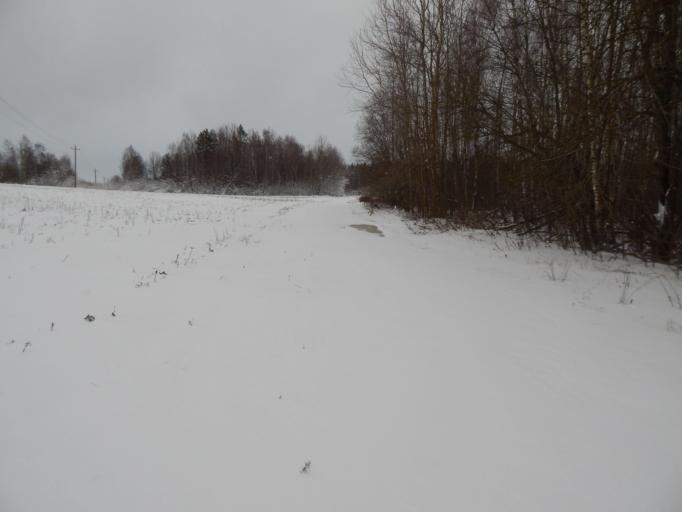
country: BY
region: Minsk
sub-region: Minski Rayon
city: Krasnaye
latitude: 54.1310
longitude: 27.0826
